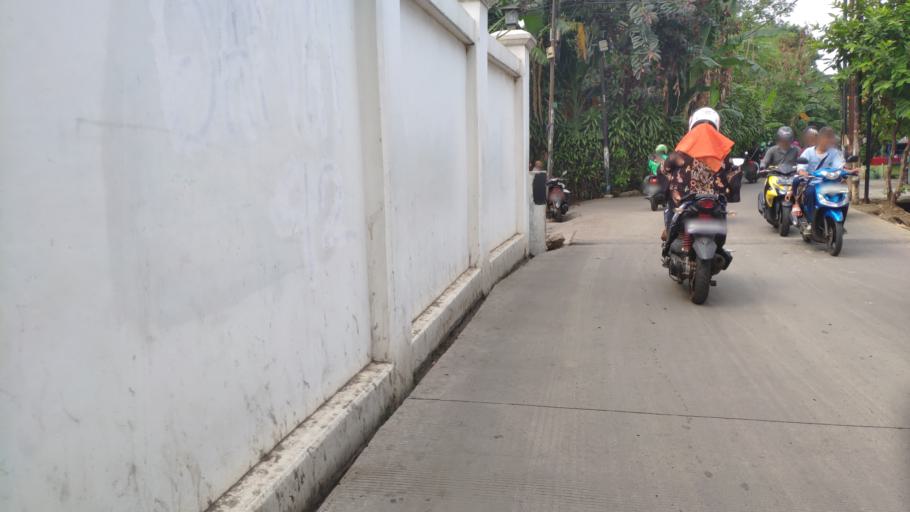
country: ID
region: West Java
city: Depok
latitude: -6.3406
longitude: 106.8125
